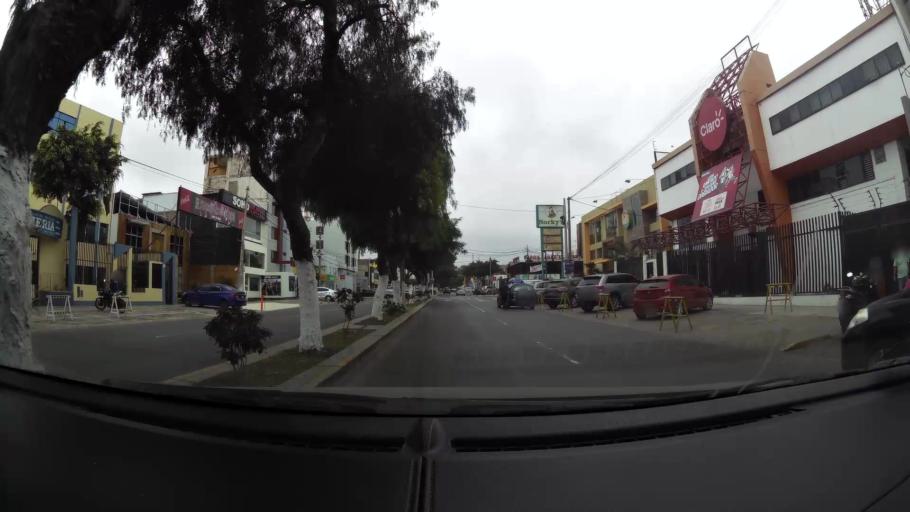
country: PE
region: La Libertad
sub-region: Provincia de Trujillo
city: Trujillo
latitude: -8.1220
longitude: -79.0366
